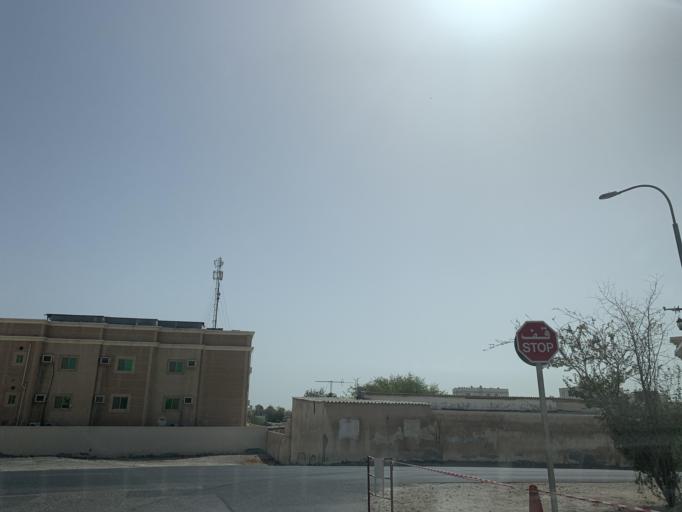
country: BH
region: Northern
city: Ar Rifa'
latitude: 26.1515
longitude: 50.5773
